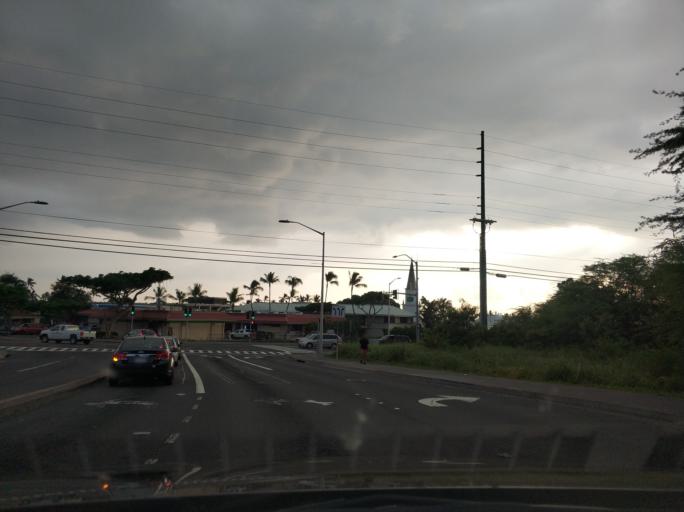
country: US
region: Hawaii
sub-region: Hawaii County
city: Kailua-Kona
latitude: 19.6412
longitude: -155.9925
